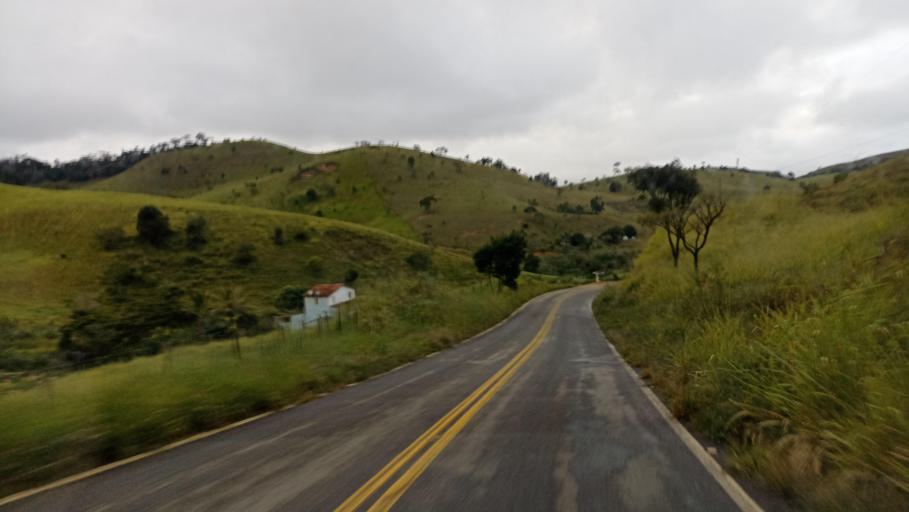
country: BR
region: Bahia
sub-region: Itanhem
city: Itanhem
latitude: -16.6907
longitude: -40.5099
